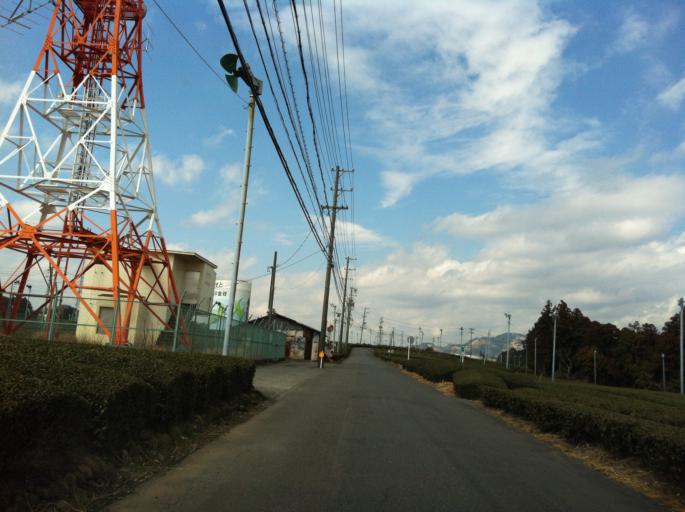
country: JP
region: Shizuoka
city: Kanaya
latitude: 34.8119
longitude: 138.1274
